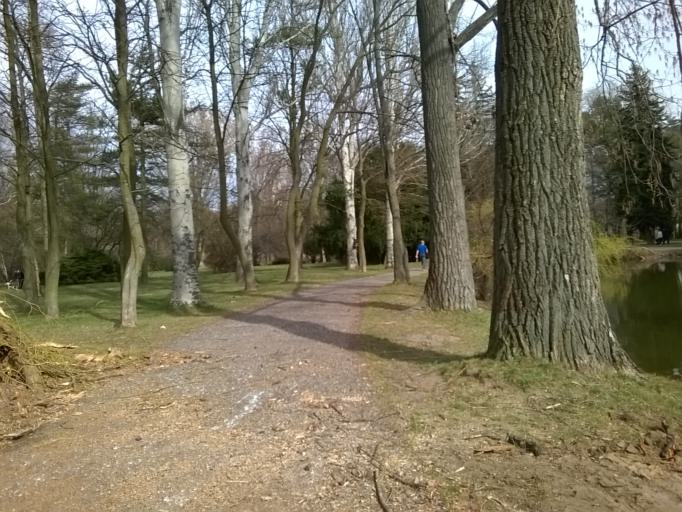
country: SK
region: Nitriansky
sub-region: Okres Nitra
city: Nitra
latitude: 48.3160
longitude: 18.0792
